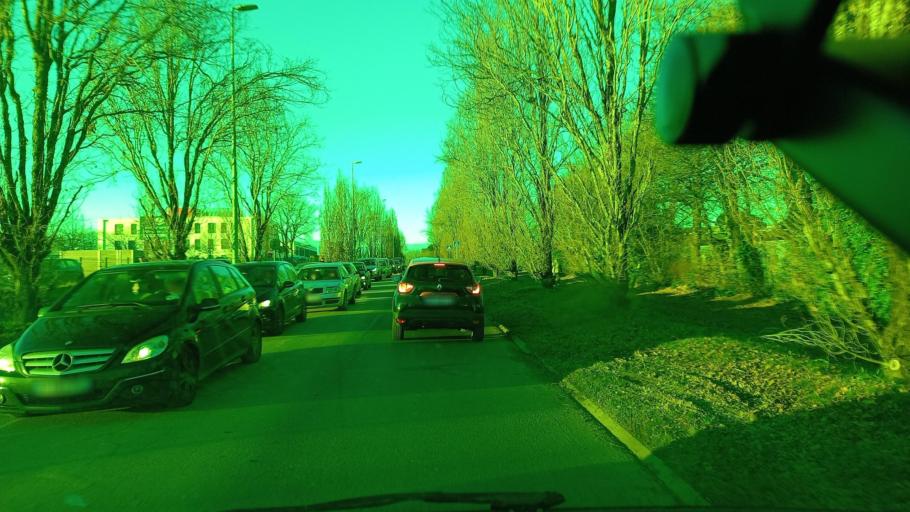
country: FR
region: Pays de la Loire
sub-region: Departement de la Vendee
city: La Roche-sur-Yon
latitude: 46.6562
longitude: -1.4108
